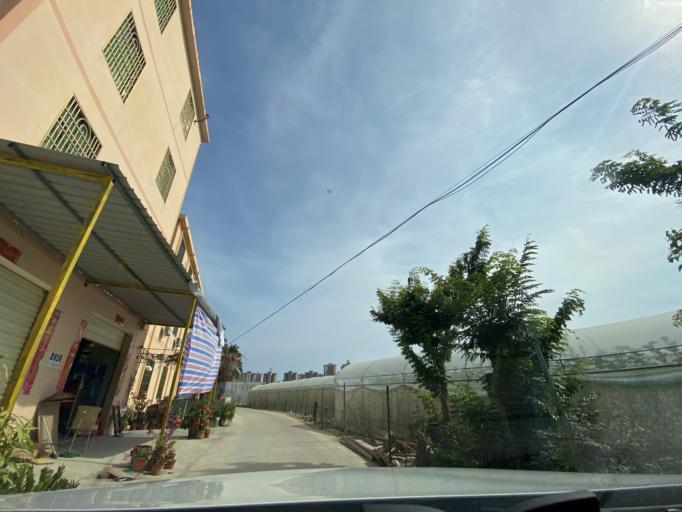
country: CN
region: Hainan
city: Yingzhou
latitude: 18.4068
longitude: 109.8311
